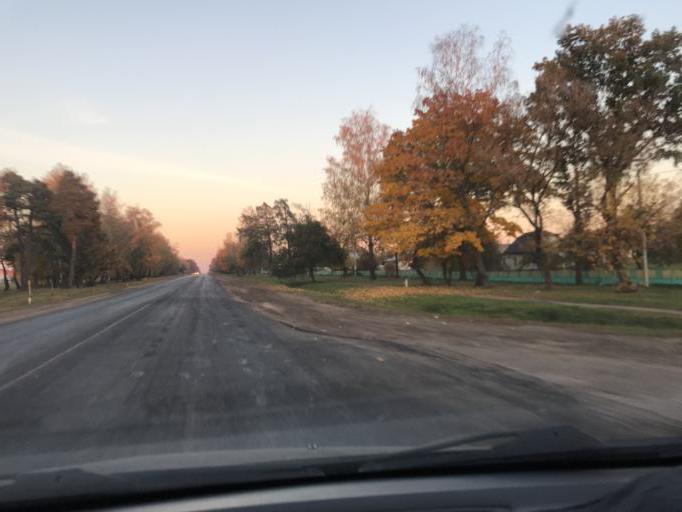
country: BY
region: Mogilev
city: Hlusha
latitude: 53.0982
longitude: 29.0094
